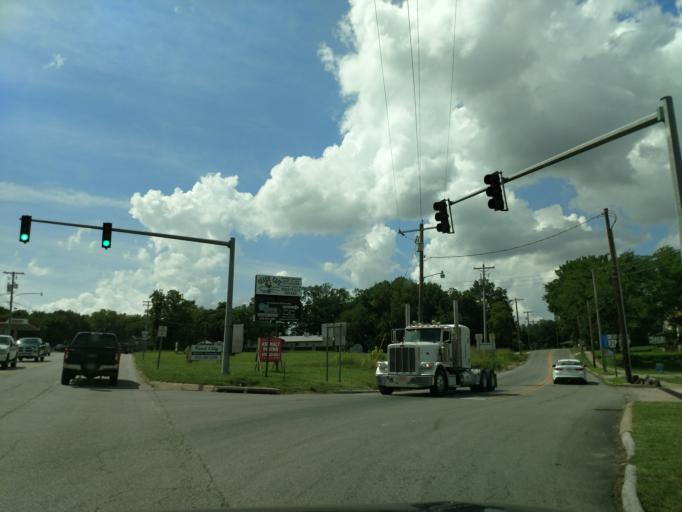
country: US
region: Arkansas
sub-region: Carroll County
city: Berryville
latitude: 36.3607
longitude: -93.5641
